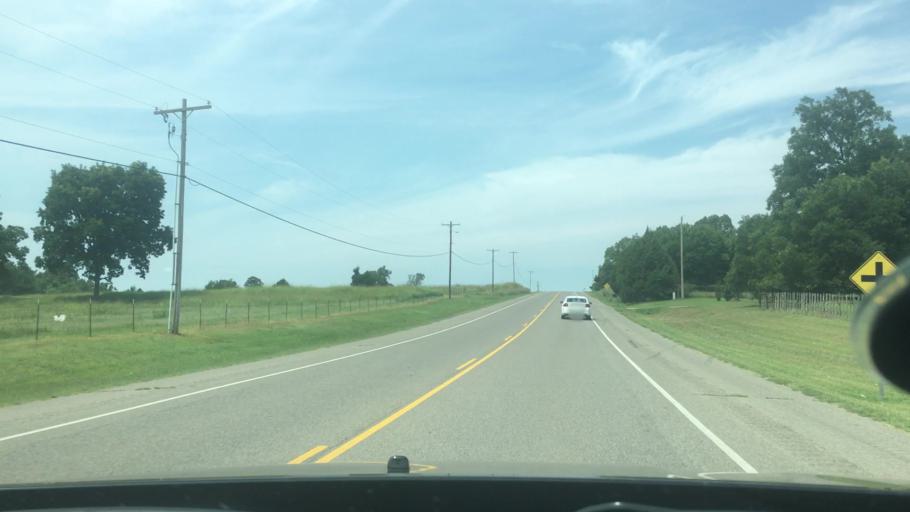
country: US
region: Oklahoma
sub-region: Pottawatomie County
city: Shawnee
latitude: 35.3331
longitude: -96.8175
